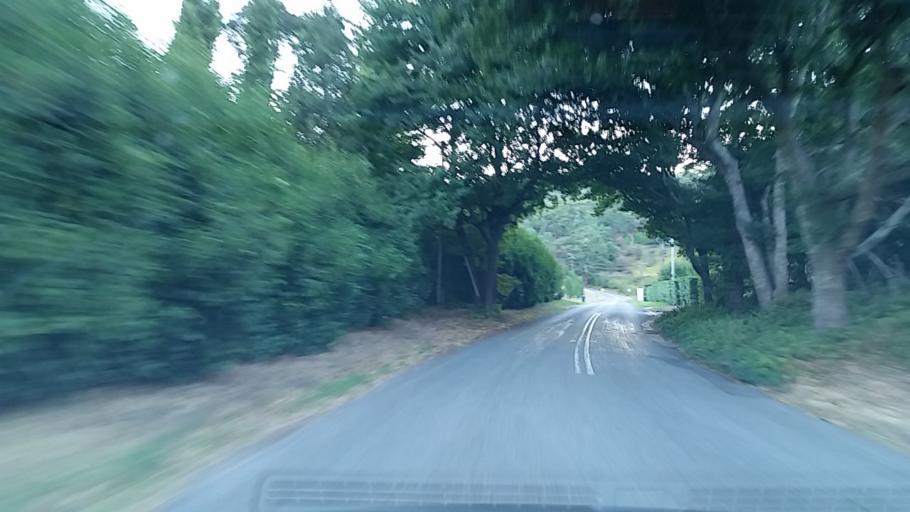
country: AU
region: South Australia
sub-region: Adelaide Hills
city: Adelaide Hills
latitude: -34.8838
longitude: 138.7518
